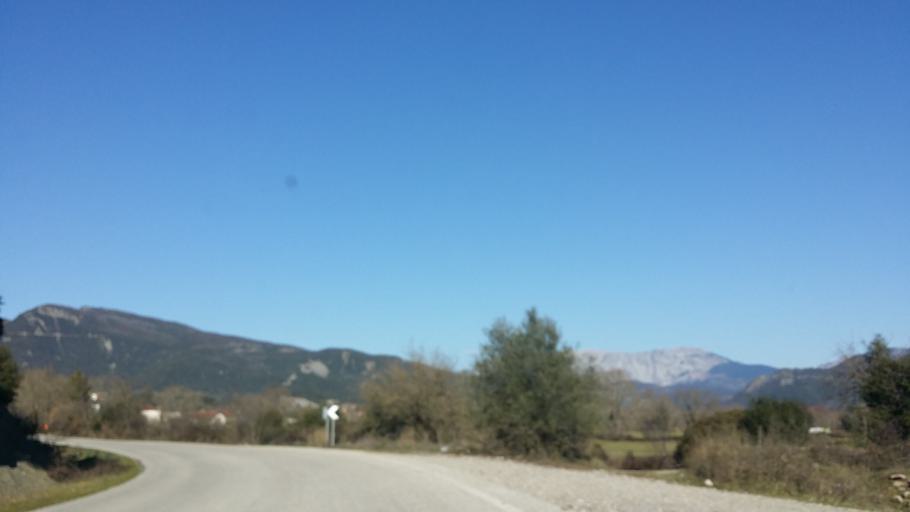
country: GR
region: West Greece
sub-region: Nomos Aitolias kai Akarnanias
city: Sardinia
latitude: 38.8604
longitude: 21.3394
